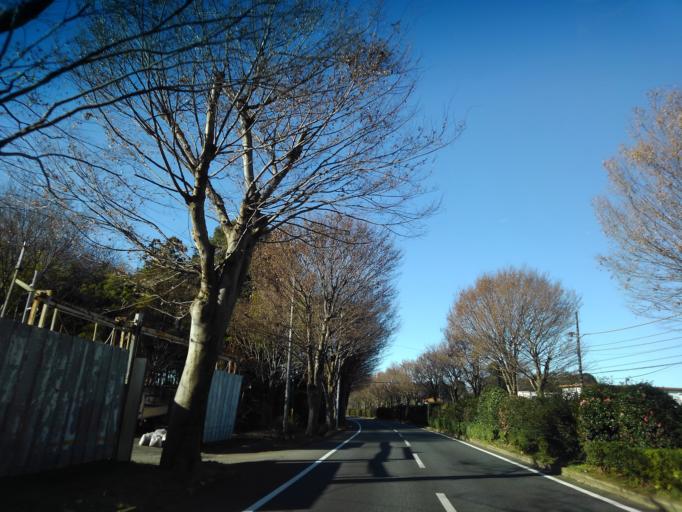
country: JP
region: Saitama
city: Oi
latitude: 35.8086
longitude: 139.5161
